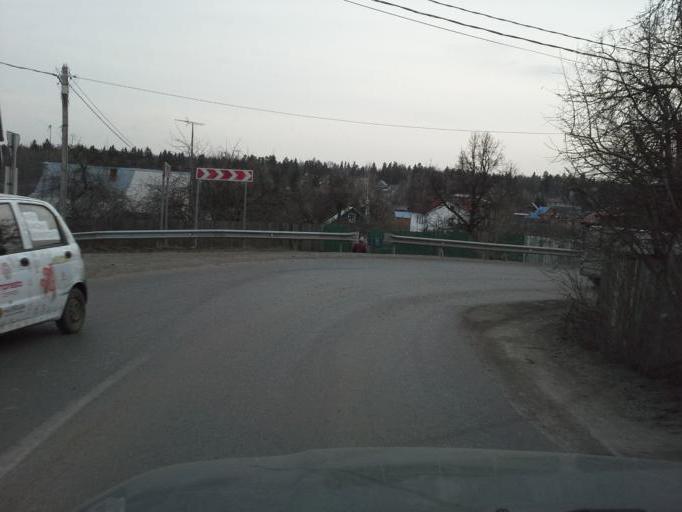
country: RU
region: Moskovskaya
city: Lesnoy Gorodok
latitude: 55.6493
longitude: 37.2107
